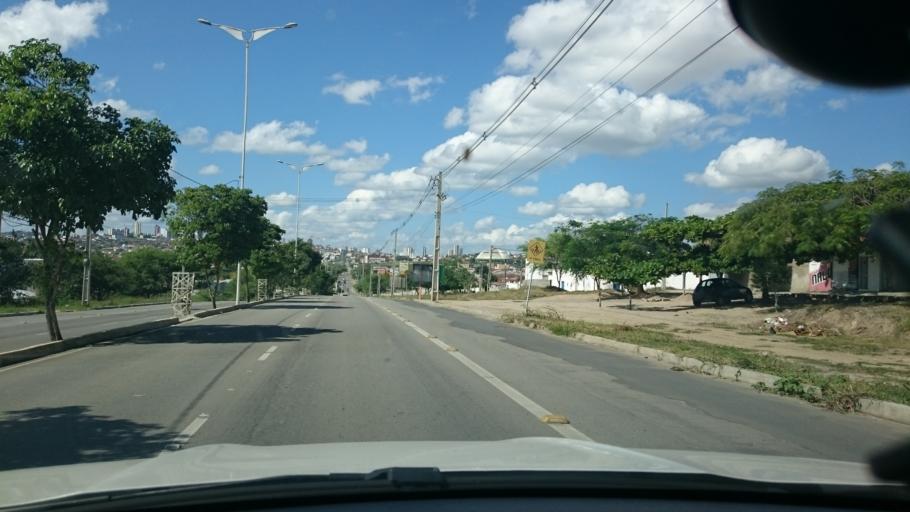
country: BR
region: Paraiba
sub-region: Campina Grande
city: Campina Grande
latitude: -7.2387
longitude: -35.9265
